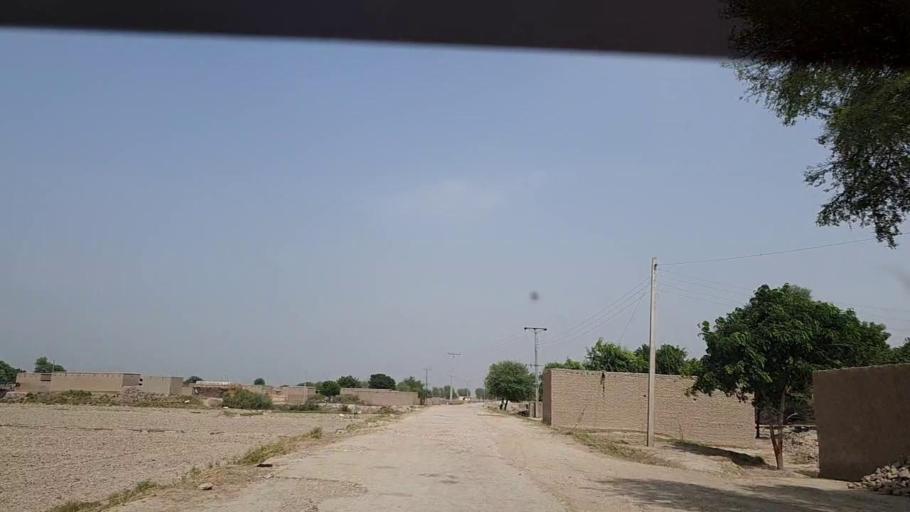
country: PK
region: Sindh
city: Khairpur Nathan Shah
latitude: 27.0810
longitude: 67.6743
